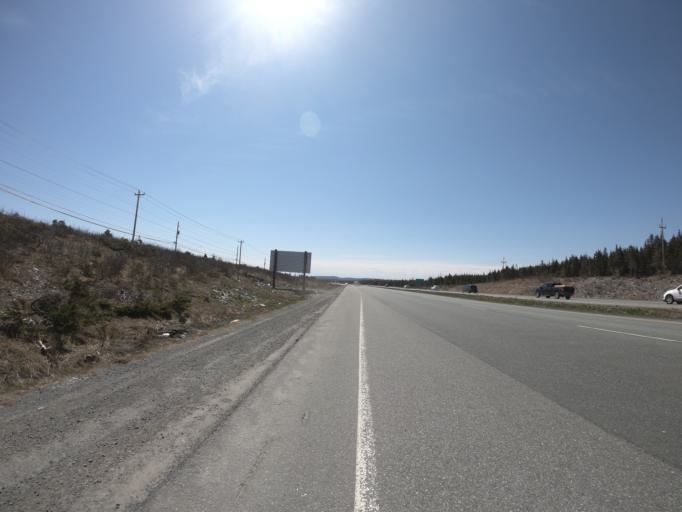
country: CA
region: Newfoundland and Labrador
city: Mount Pearl
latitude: 47.5048
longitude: -52.8206
